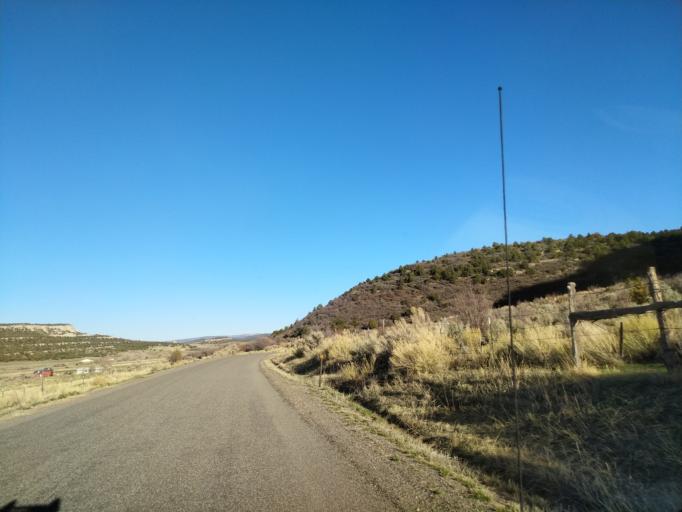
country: US
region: Colorado
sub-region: Mesa County
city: Loma
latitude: 38.9527
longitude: -108.9937
